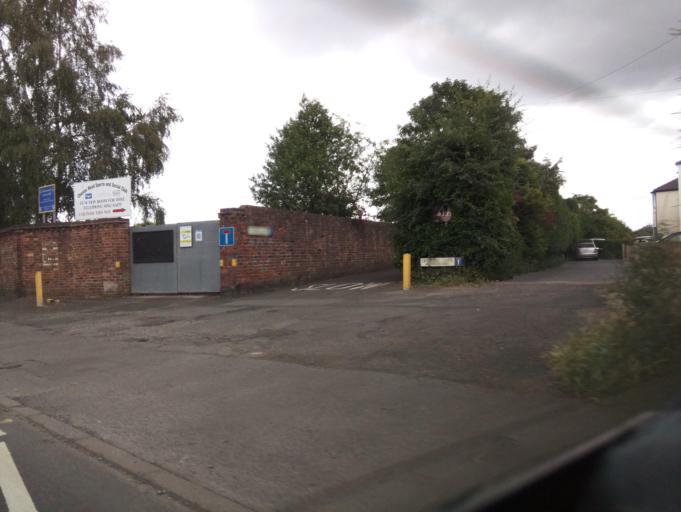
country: GB
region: England
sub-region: Worcestershire
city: Kidderminster
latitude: 52.3882
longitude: -2.2333
